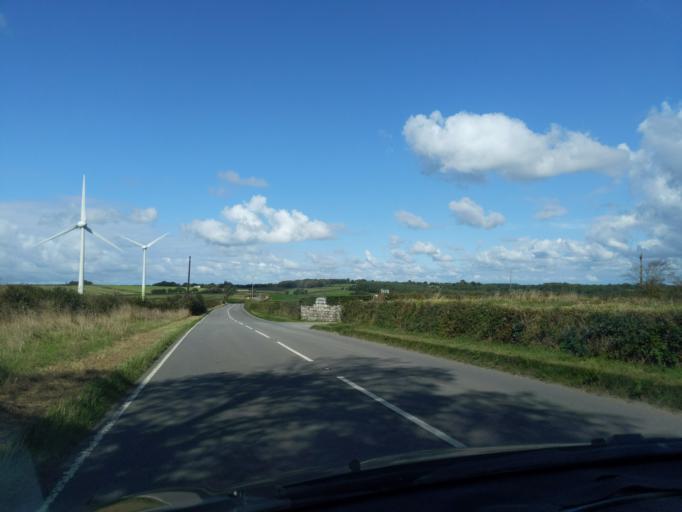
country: GB
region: England
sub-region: Cornwall
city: Boyton
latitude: 50.7389
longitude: -4.3227
